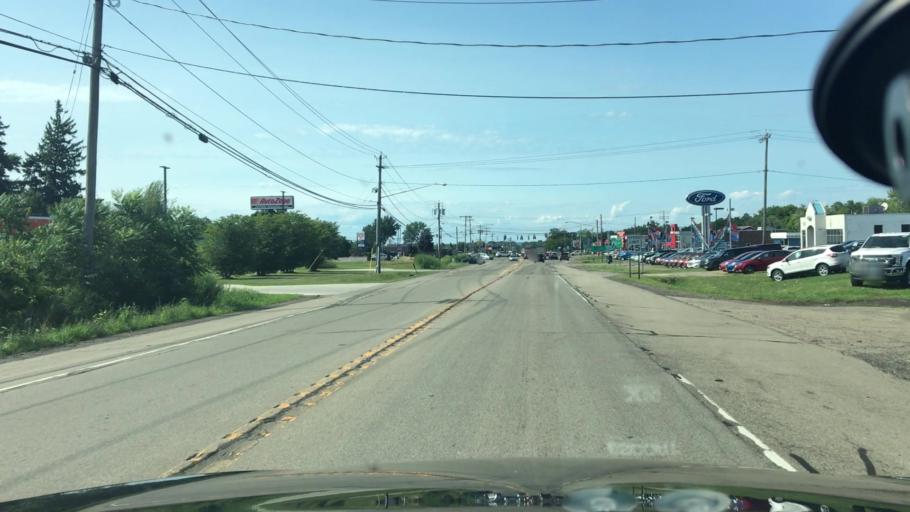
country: US
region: New York
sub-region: Chautauqua County
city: Fredonia
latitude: 42.4484
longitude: -79.3068
